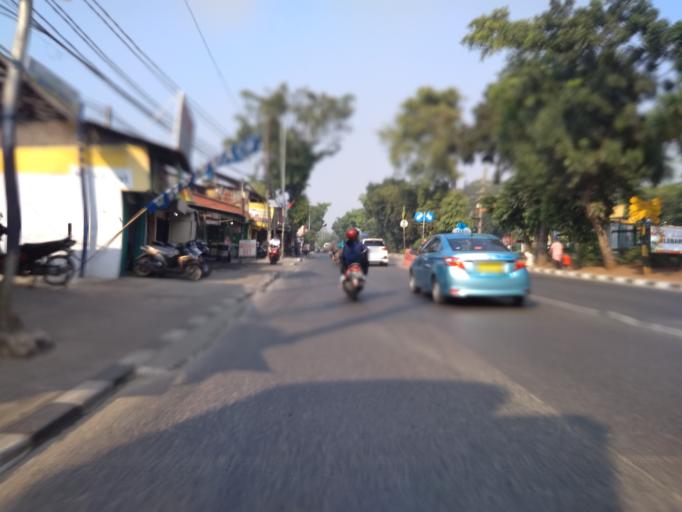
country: ID
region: West Java
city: Depok
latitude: -6.3234
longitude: 106.8354
